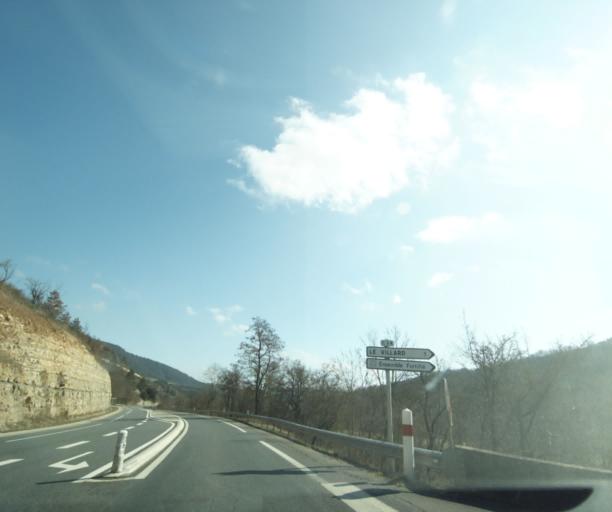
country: FR
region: Languedoc-Roussillon
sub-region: Departement de la Lozere
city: Chanac
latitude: 44.4841
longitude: 3.3001
